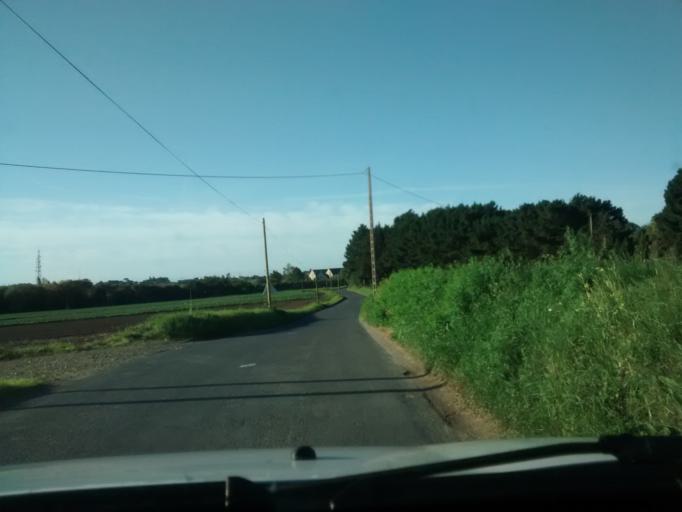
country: FR
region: Brittany
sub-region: Departement d'Ille-et-Vilaine
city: Saint-Malo
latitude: 48.6722
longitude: -1.9685
